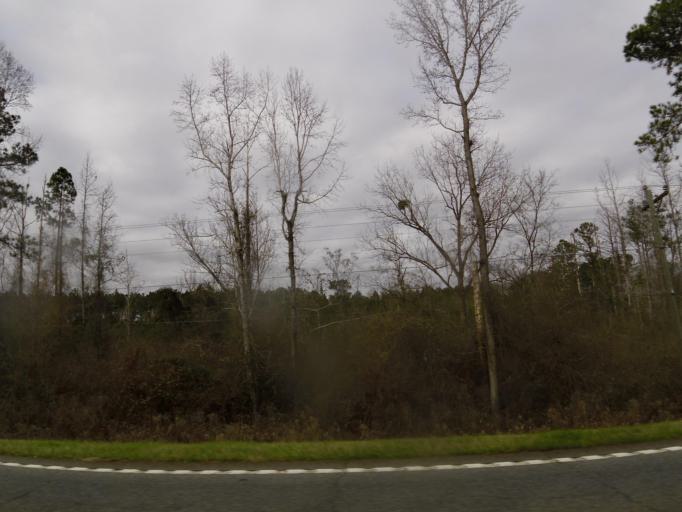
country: US
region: Georgia
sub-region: Quitman County
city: Georgetown
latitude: 31.8571
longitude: -85.0486
